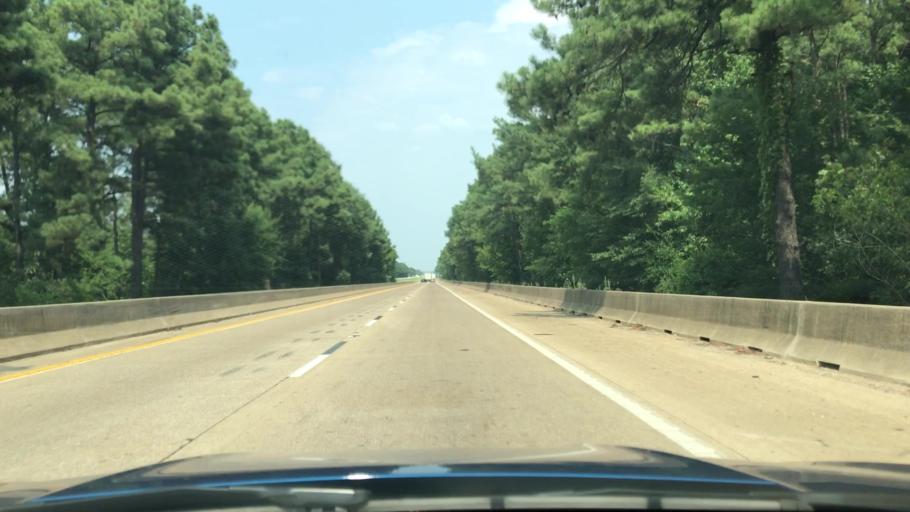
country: US
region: Texas
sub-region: Gregg County
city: Longview
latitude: 32.4331
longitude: -94.7567
